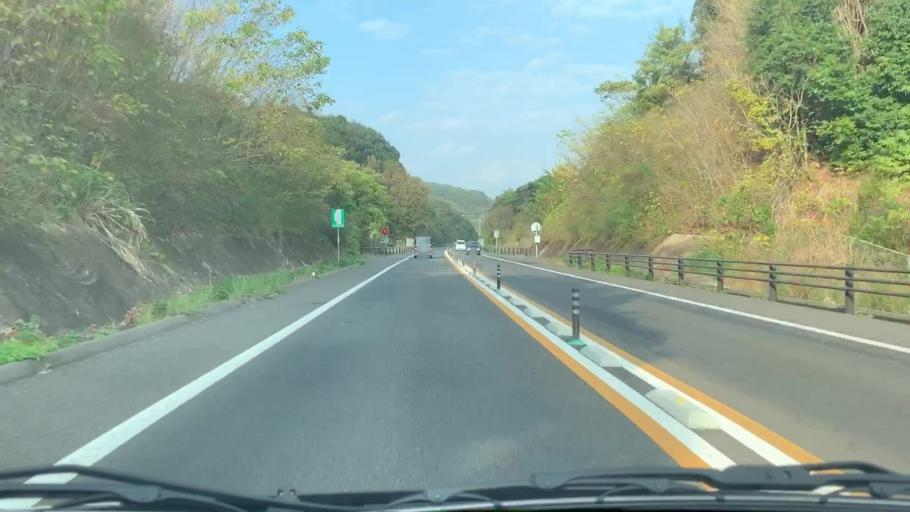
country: JP
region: Nagasaki
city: Sasebo
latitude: 33.0153
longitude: 129.7309
